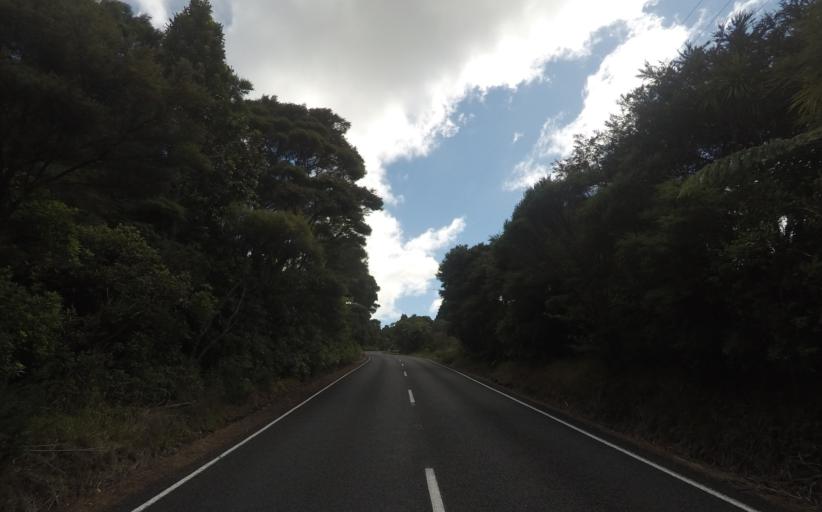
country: NZ
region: Auckland
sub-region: Auckland
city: Muriwai Beach
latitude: -36.8639
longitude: 174.5144
